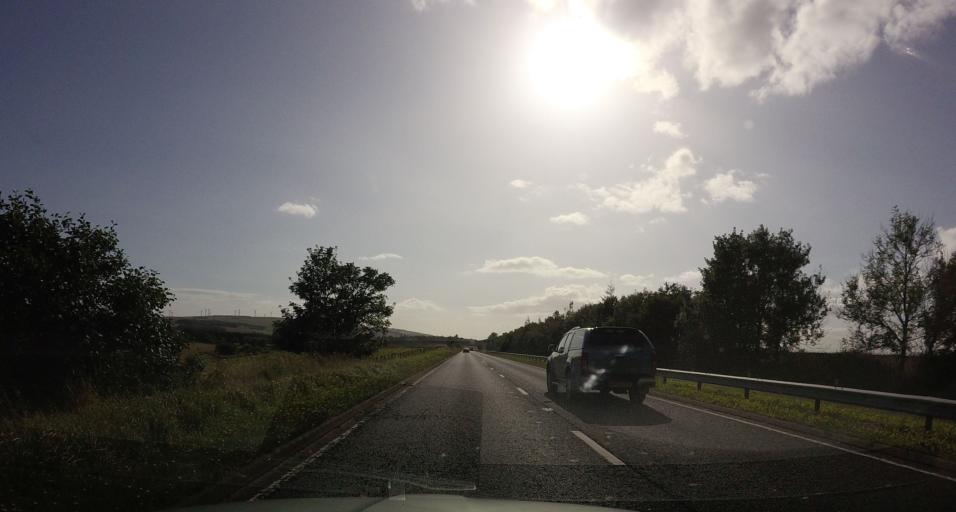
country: GB
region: Scotland
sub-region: Aberdeenshire
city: Laurencekirk
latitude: 56.8884
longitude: -2.3907
